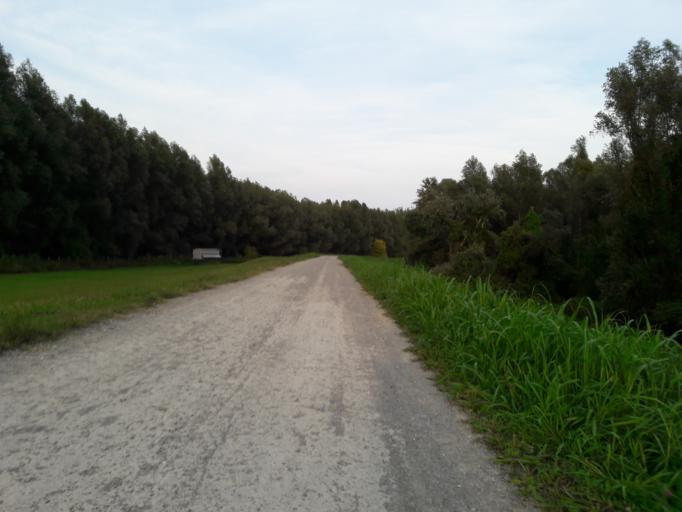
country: HR
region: Osjecko-Baranjska
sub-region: Grad Osijek
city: Osijek
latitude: 45.5668
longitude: 18.7282
